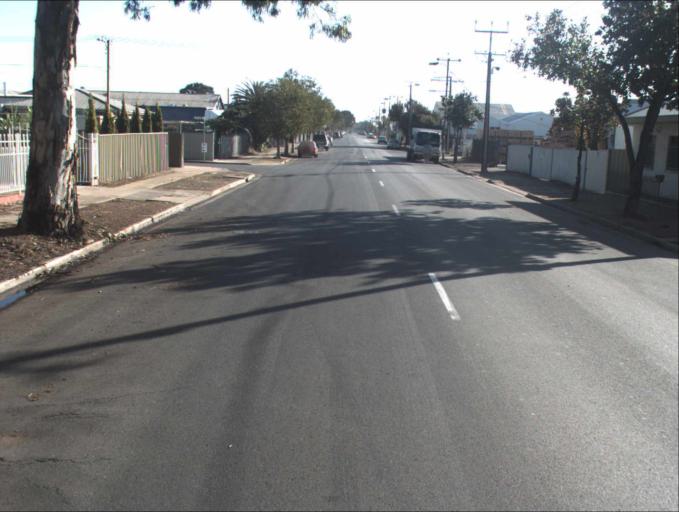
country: AU
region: South Australia
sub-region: Charles Sturt
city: Woodville North
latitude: -34.8488
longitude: 138.5511
